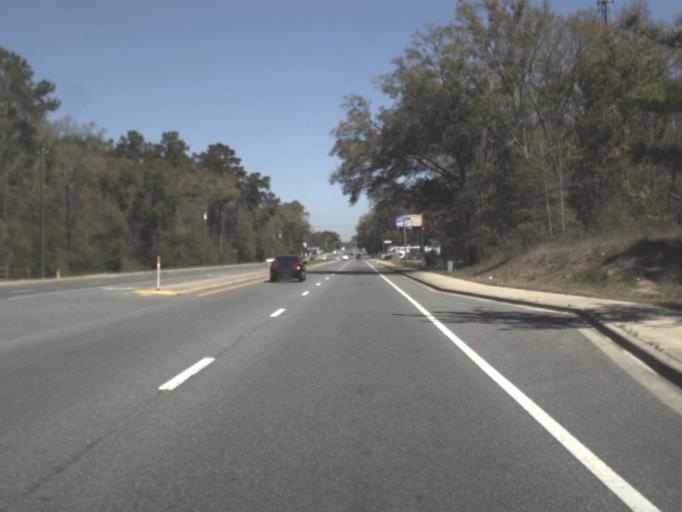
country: US
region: Florida
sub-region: Leon County
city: Woodville
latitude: 30.3652
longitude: -84.2979
